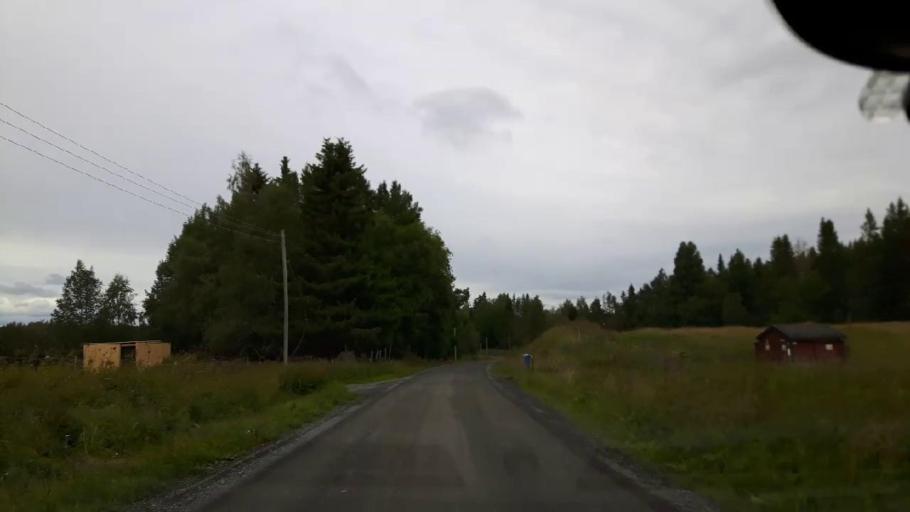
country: SE
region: Jaemtland
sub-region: Krokoms Kommun
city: Krokom
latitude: 63.2706
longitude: 14.4050
